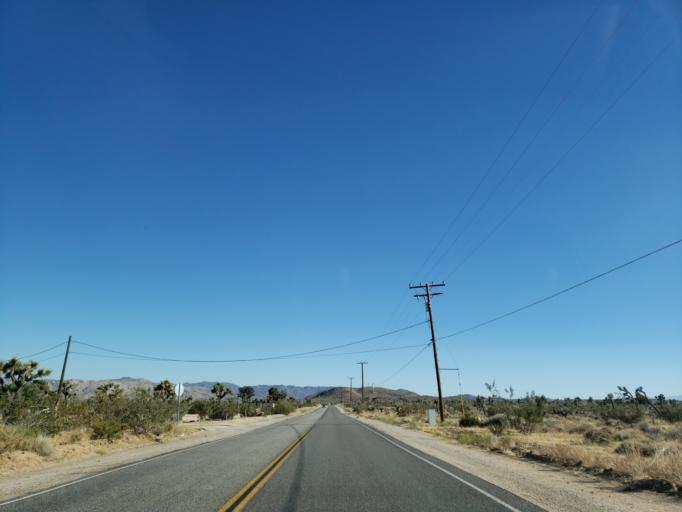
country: US
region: California
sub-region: San Bernardino County
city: Yucca Valley
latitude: 34.1815
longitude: -116.3871
